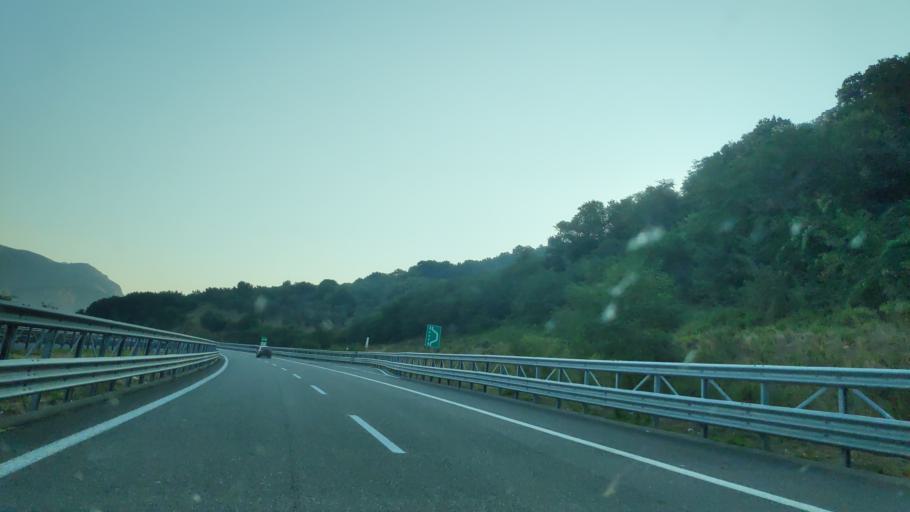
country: IT
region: Calabria
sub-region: Provincia di Catanzaro
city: Nocera Terinese
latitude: 39.0421
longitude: 16.1439
